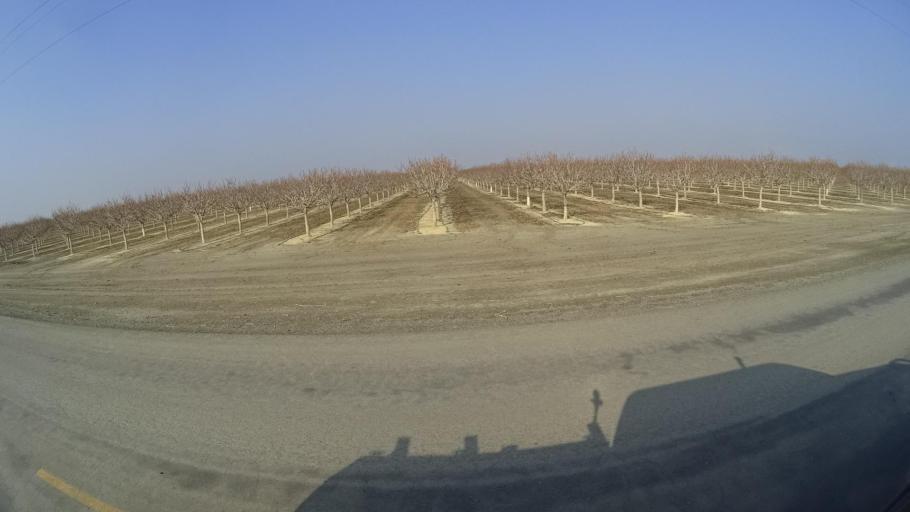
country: US
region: California
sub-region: Kern County
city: Greenfield
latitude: 35.1514
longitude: -119.0812
